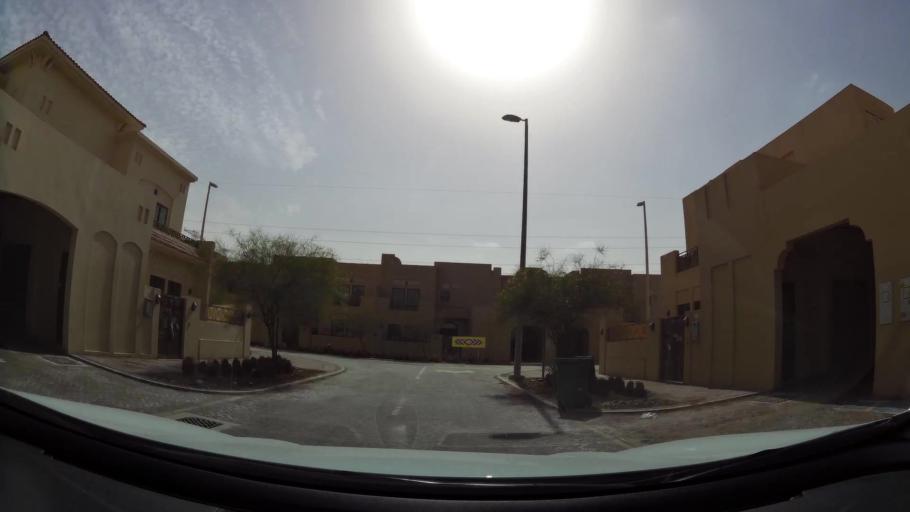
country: AE
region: Abu Dhabi
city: Abu Dhabi
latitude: 24.4065
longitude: 54.5333
